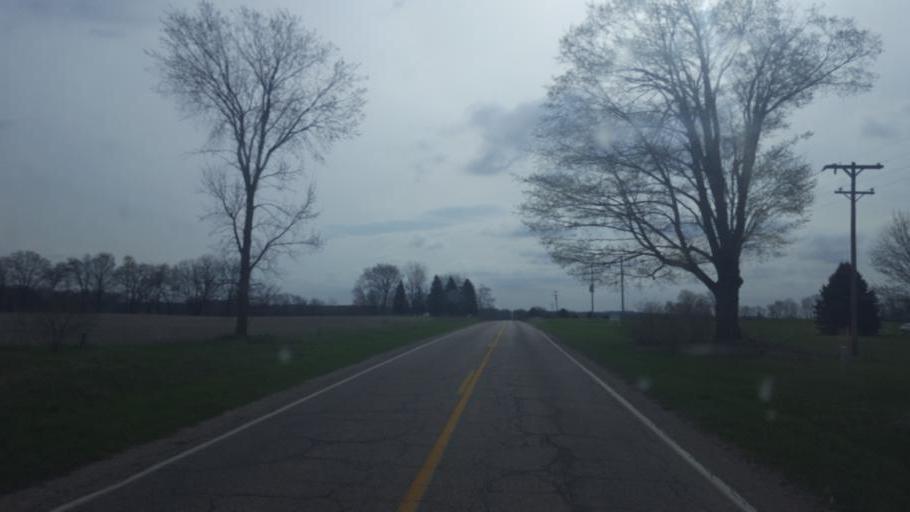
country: US
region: Michigan
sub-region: Isabella County
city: Lake Isabella
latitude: 43.5250
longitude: -84.9415
